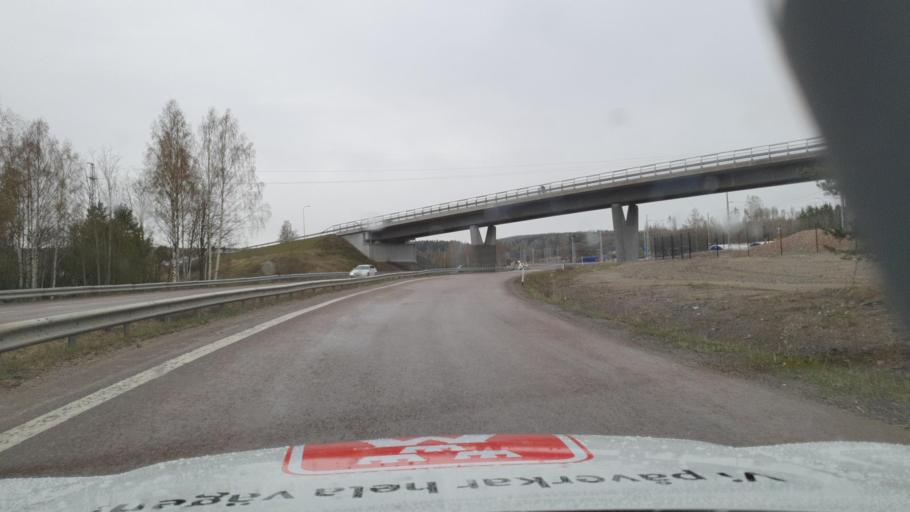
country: SE
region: Vaesternorrland
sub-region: Sundsvalls Kommun
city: Sundsvall
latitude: 62.4066
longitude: 17.2331
